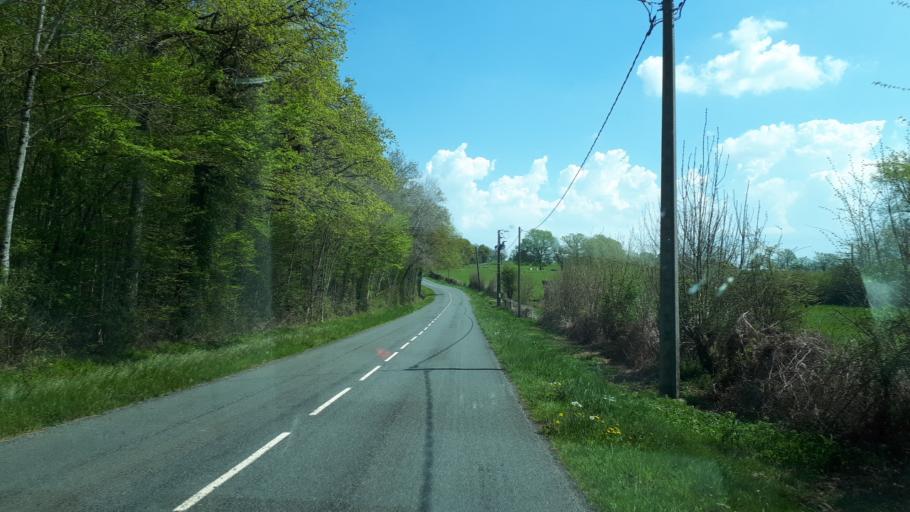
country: FR
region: Centre
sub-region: Departement du Cher
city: Rians
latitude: 47.3002
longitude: 2.6592
